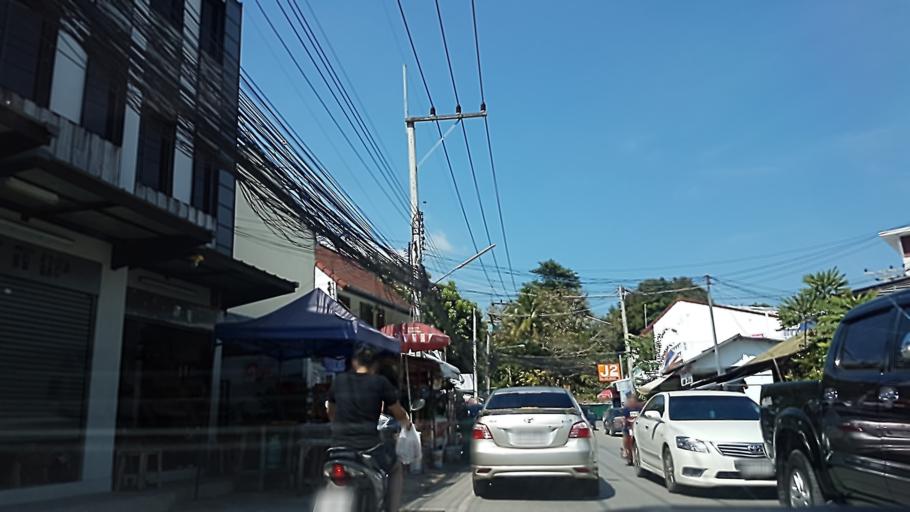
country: TH
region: Chiang Mai
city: Chiang Mai
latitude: 18.8136
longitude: 98.9570
